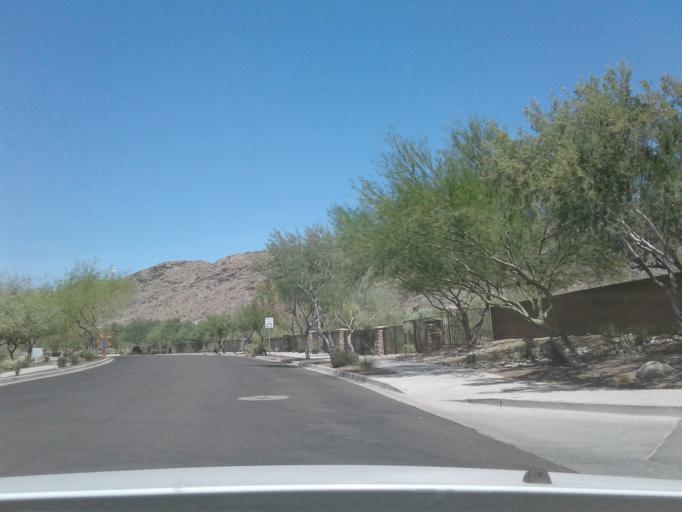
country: US
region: Arizona
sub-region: Maricopa County
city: Laveen
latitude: 33.2964
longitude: -112.1203
